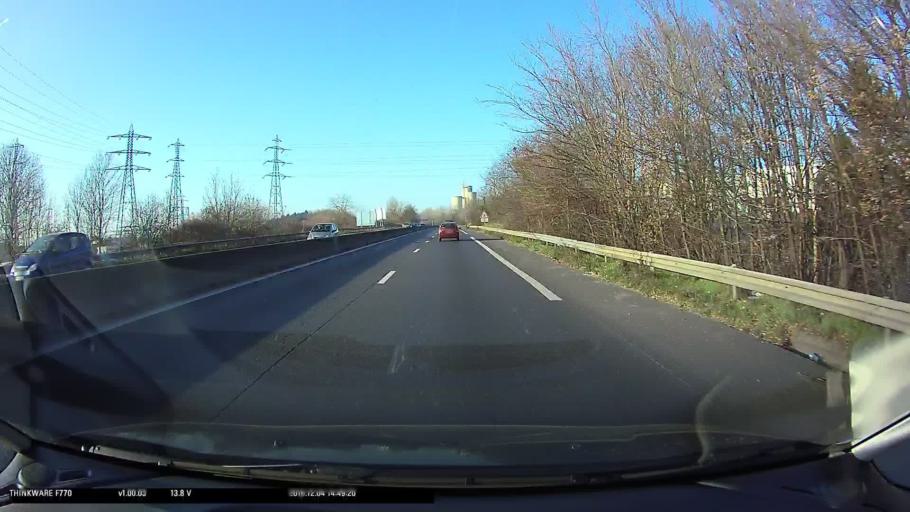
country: FR
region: Ile-de-France
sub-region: Departement du Val-d'Oise
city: Cergy-Pontoise
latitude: 49.0474
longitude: 2.0722
